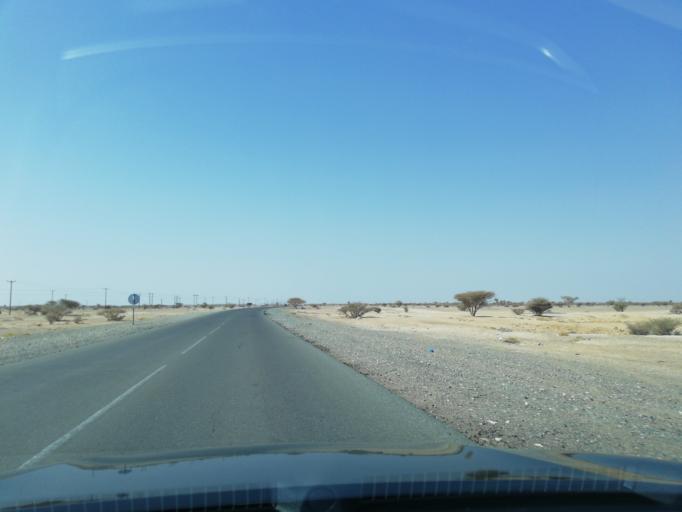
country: OM
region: Muhafazat ad Dakhiliyah
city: Adam
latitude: 22.3448
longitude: 58.0692
